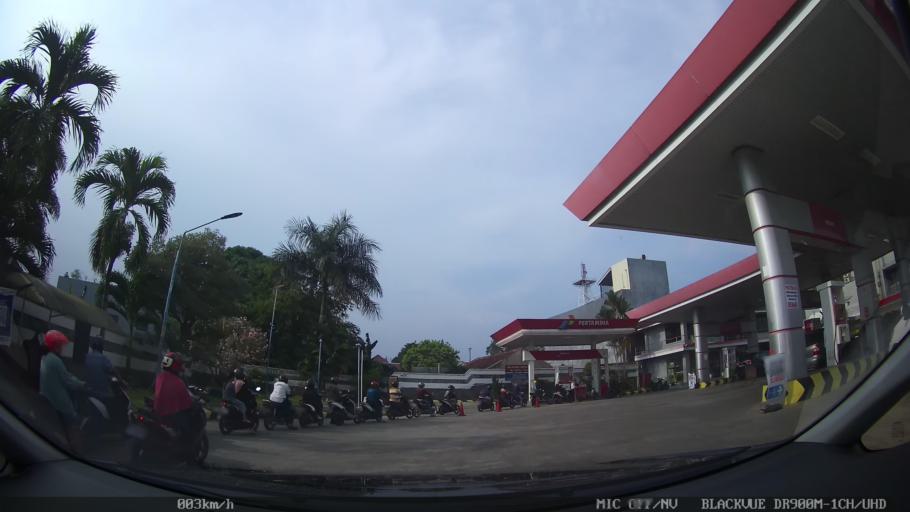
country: ID
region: Lampung
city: Bandarlampung
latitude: -5.4230
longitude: 105.2714
